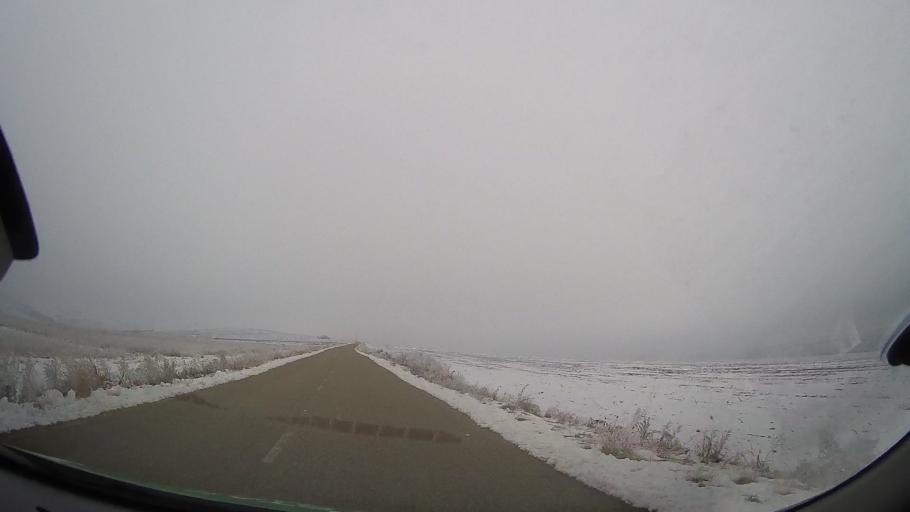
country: RO
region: Vaslui
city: Coroiesti
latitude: 46.2246
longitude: 27.4786
